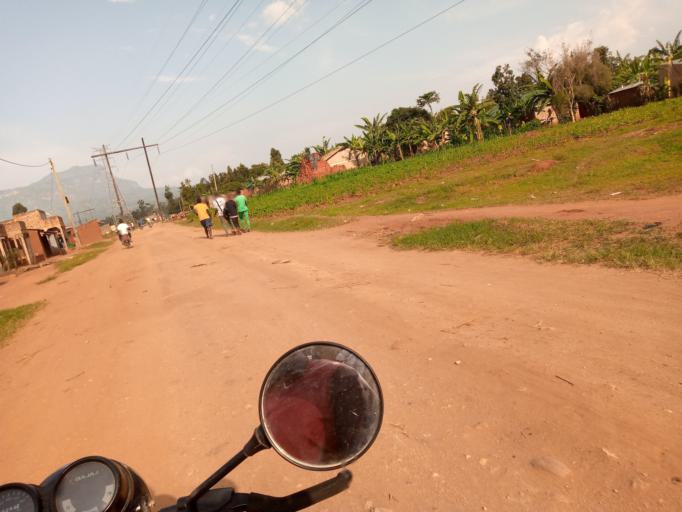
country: UG
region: Eastern Region
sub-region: Mbale District
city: Mbale
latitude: 1.0583
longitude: 34.1572
